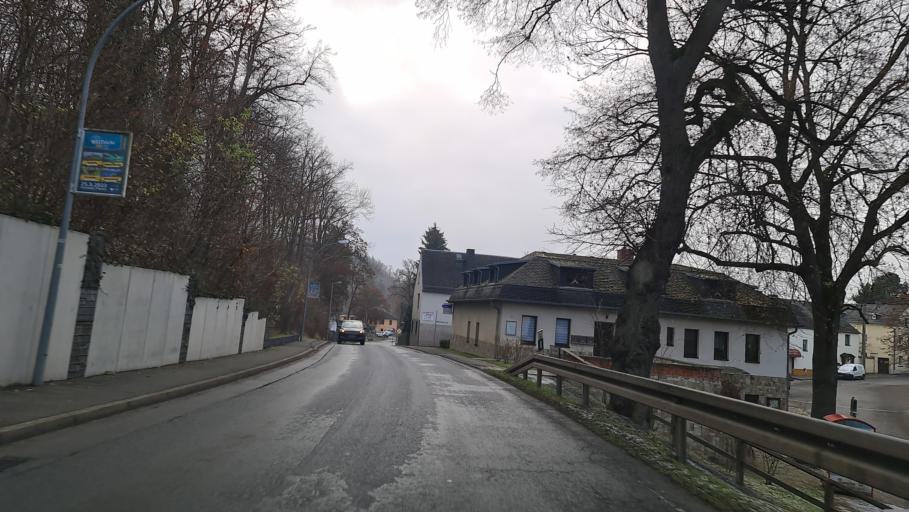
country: DE
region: Saxony
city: Weischlitz
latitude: 50.4768
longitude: 12.0862
